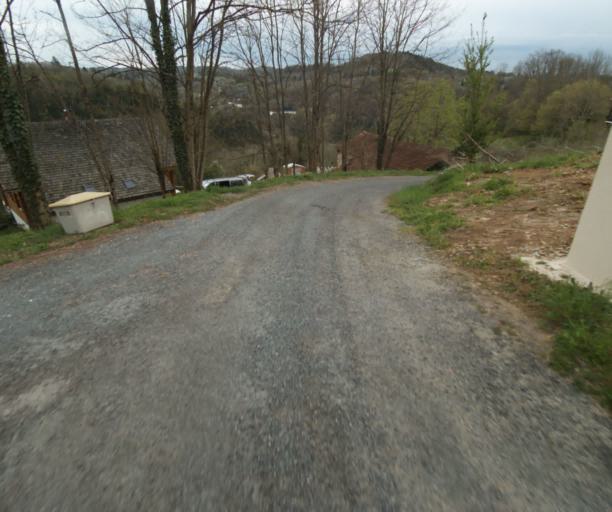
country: FR
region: Limousin
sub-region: Departement de la Correze
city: Laguenne
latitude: 45.2530
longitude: 1.7717
